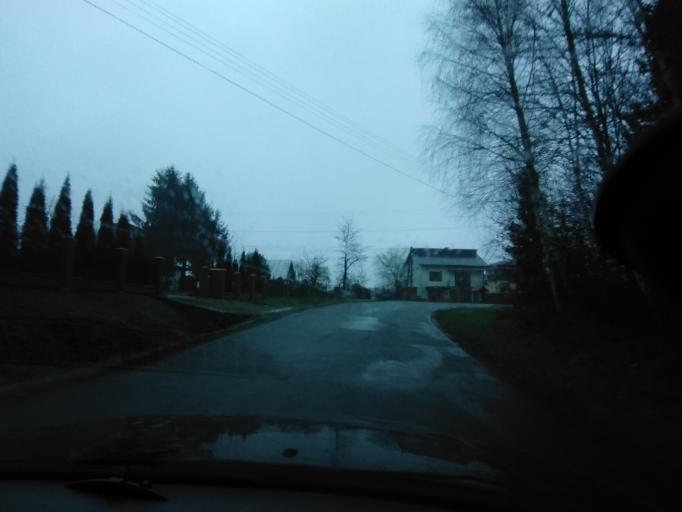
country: PL
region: Subcarpathian Voivodeship
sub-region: Powiat brzozowski
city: Jablonka
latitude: 49.7366
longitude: 22.0932
